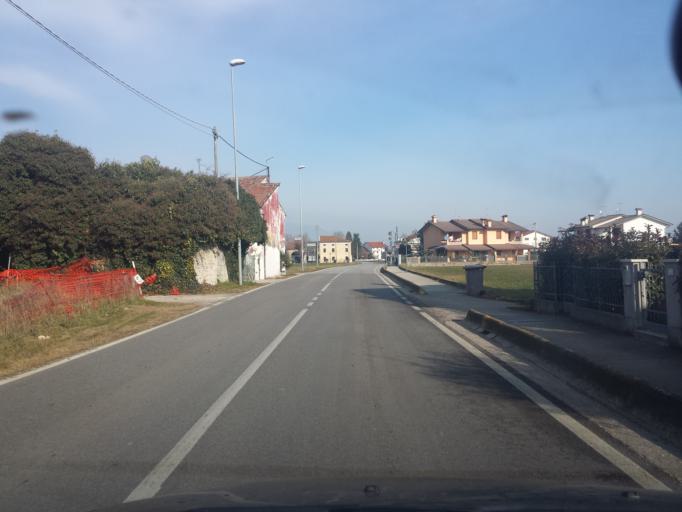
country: IT
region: Veneto
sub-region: Provincia di Vicenza
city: Bressanvido
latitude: 45.6520
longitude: 11.6389
